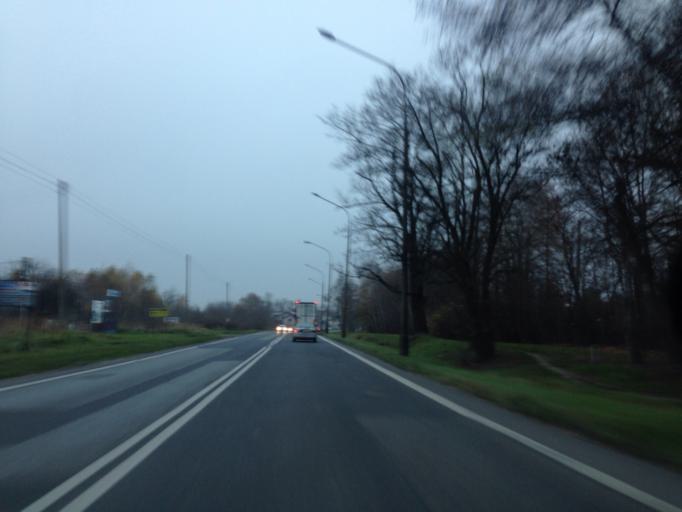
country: PL
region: Lodz Voivodeship
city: Lodz
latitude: 51.8045
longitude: 19.4958
